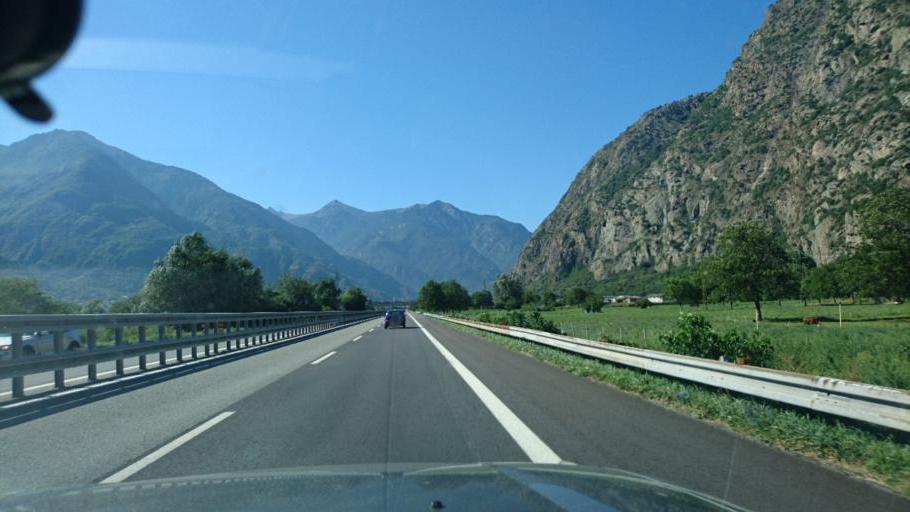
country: IT
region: Aosta Valley
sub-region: Valle d'Aosta
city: Arnad
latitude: 45.6476
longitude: 7.7094
